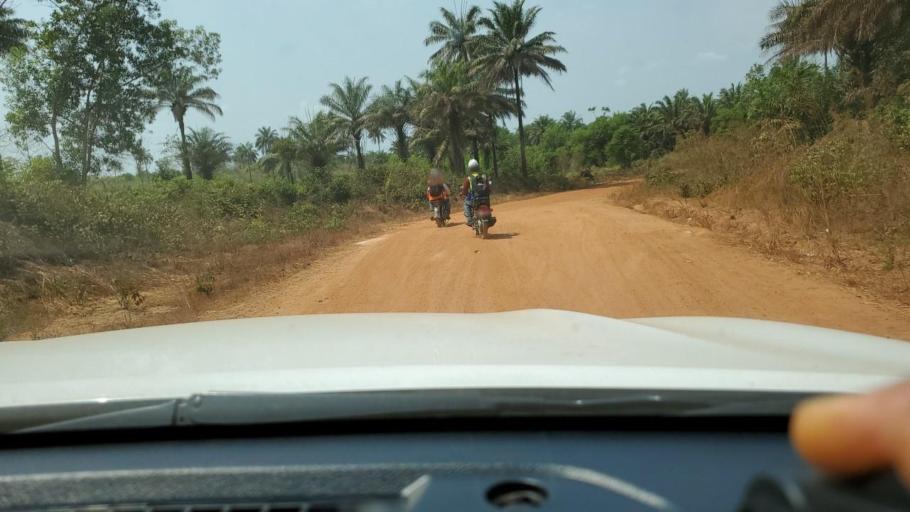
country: GN
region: Boke
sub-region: Boffa
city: Boffa
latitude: 10.0991
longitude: -13.8550
